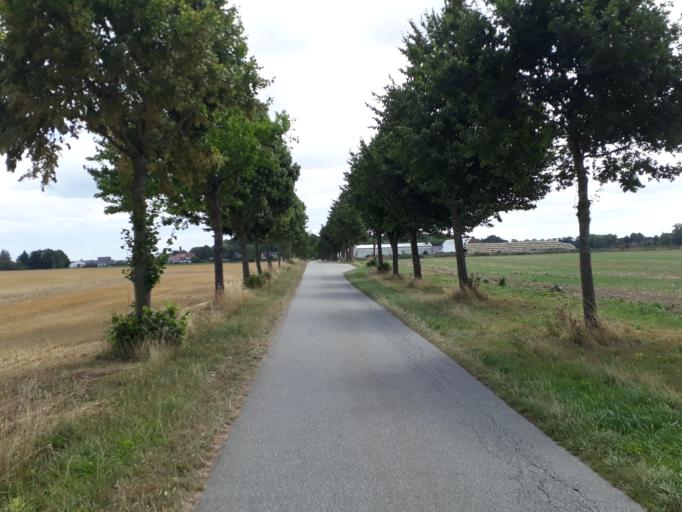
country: DE
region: Mecklenburg-Vorpommern
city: Marlow
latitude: 54.2289
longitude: 12.5453
